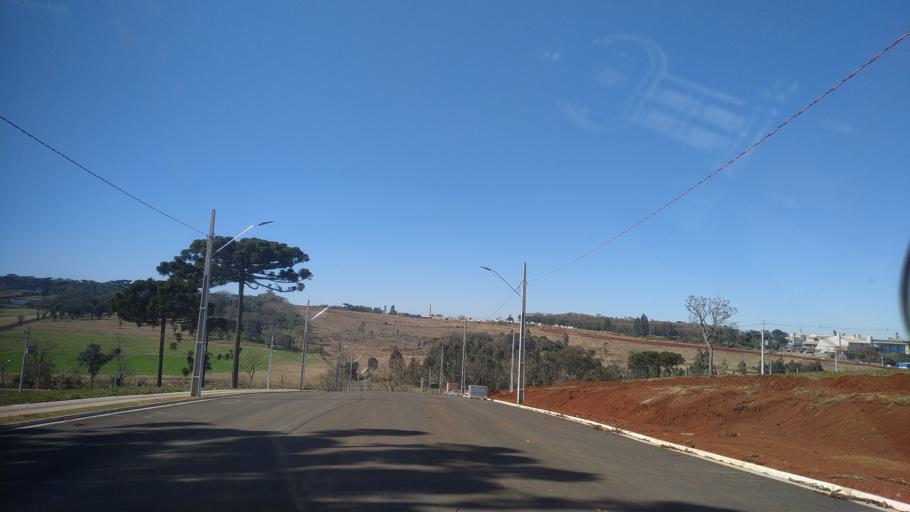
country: BR
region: Santa Catarina
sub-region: Chapeco
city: Chapeco
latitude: -27.0891
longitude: -52.7074
